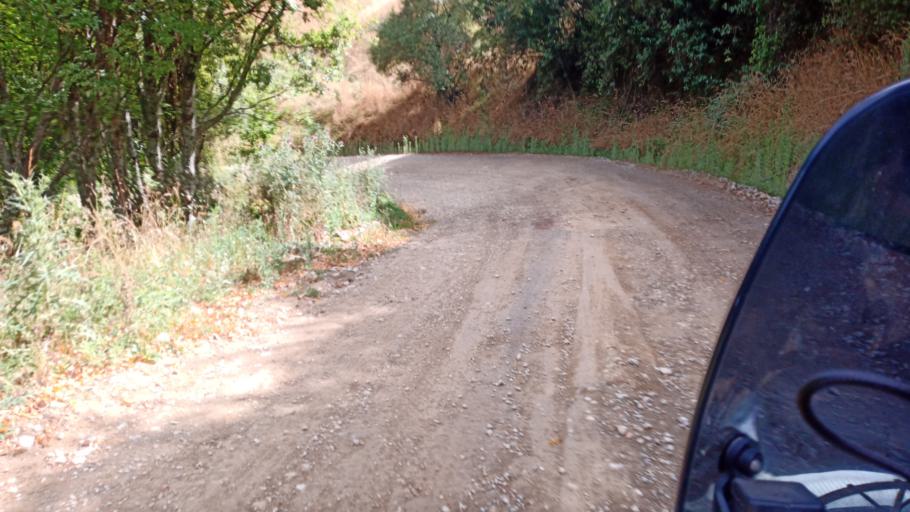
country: NZ
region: Hawke's Bay
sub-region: Wairoa District
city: Wairoa
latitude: -38.6102
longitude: 177.4416
